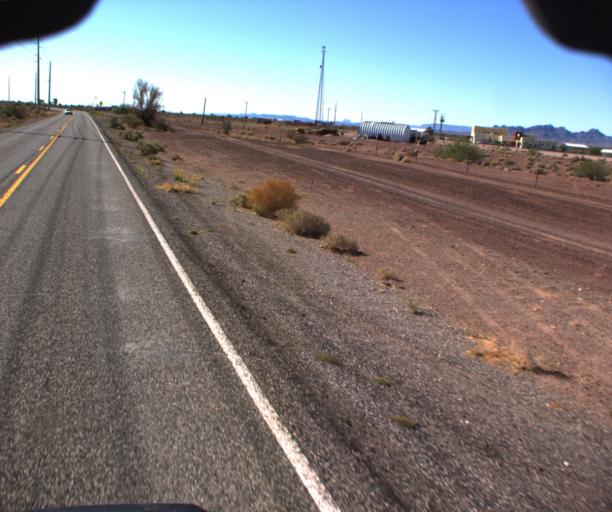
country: US
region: Arizona
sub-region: La Paz County
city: Quartzsite
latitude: 33.9159
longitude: -113.9929
